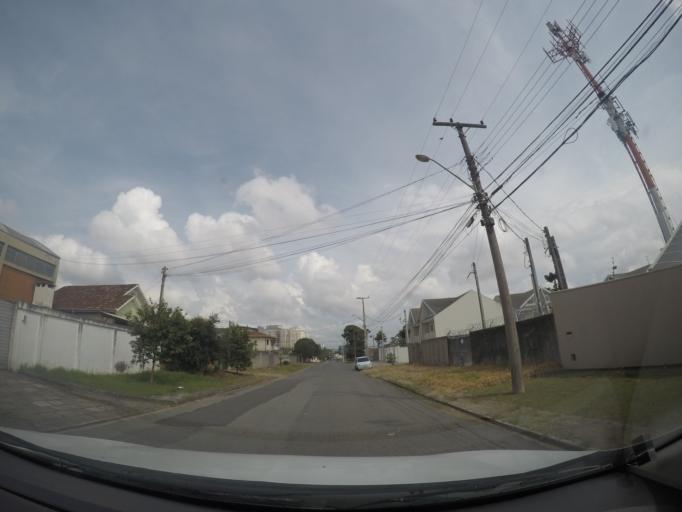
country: BR
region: Parana
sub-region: Curitiba
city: Curitiba
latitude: -25.4886
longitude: -49.2717
